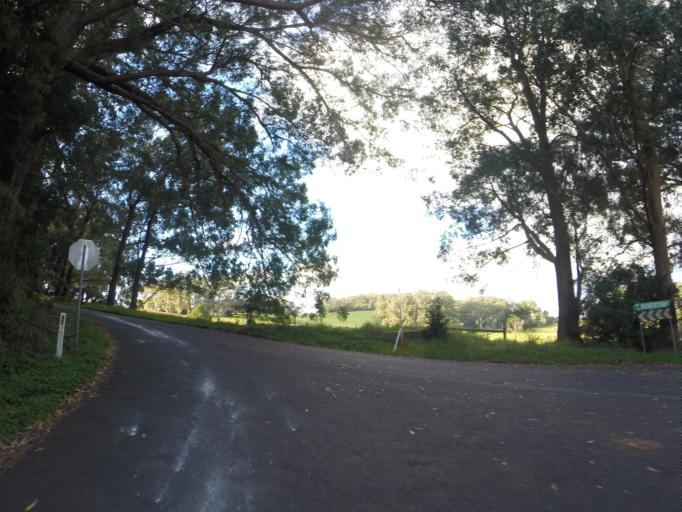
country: AU
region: New South Wales
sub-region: Shoalhaven Shire
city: Kangaroo Valley
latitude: -34.6131
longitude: 150.5351
